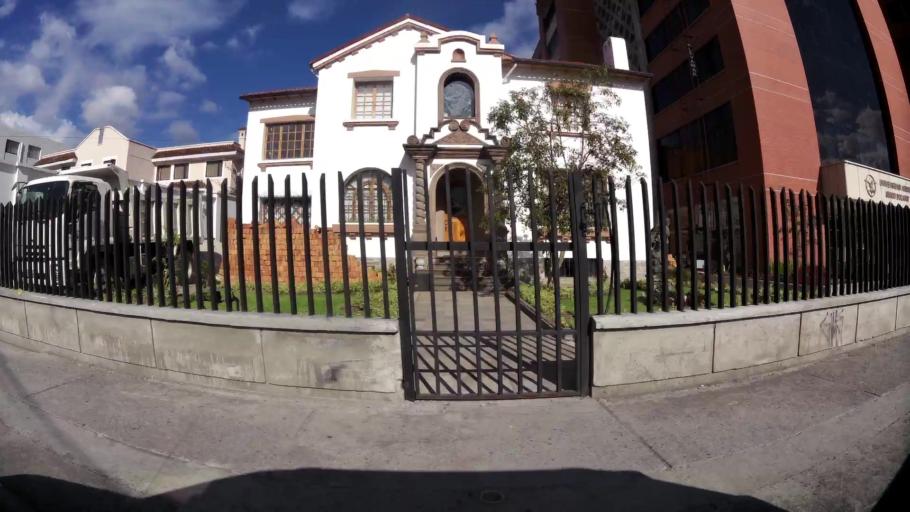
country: EC
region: Pichincha
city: Quito
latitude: -0.2107
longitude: -78.4874
